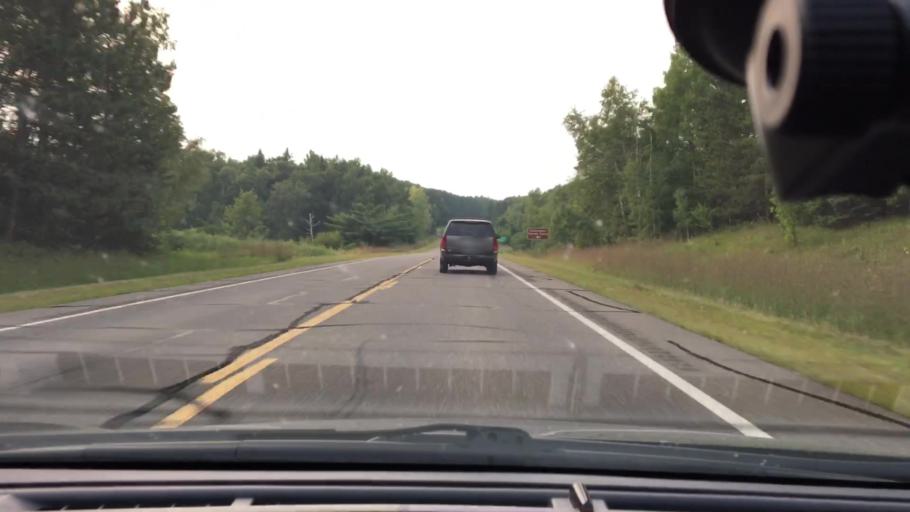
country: US
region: Minnesota
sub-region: Crow Wing County
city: Crosby
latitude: 46.3951
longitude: -93.8771
